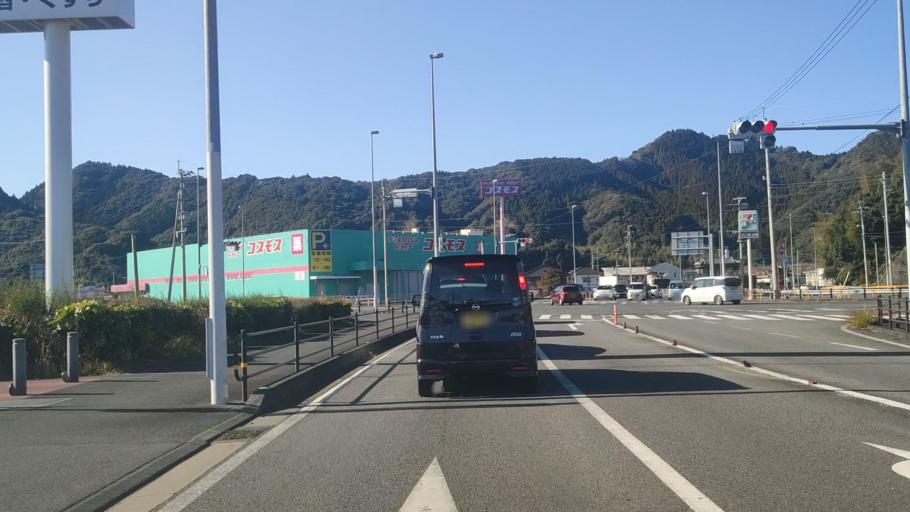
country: JP
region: Oita
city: Saiki
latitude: 32.9612
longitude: 131.8642
